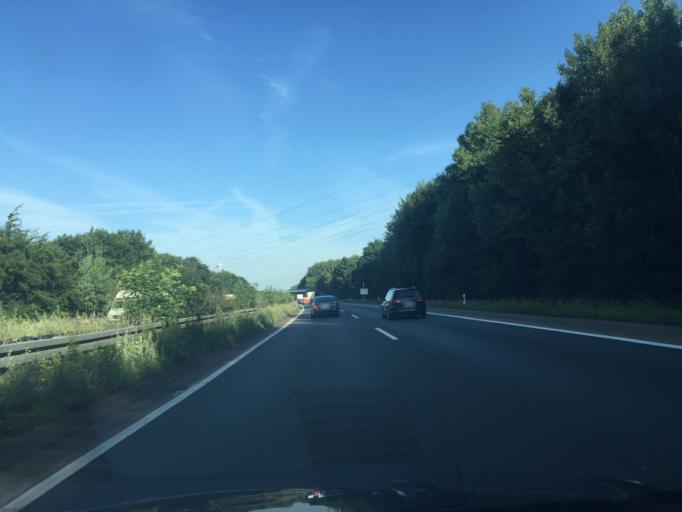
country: DE
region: North Rhine-Westphalia
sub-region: Regierungsbezirk Arnsberg
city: Nachrodt-Wiblingwerde
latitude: 51.3170
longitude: 7.5492
